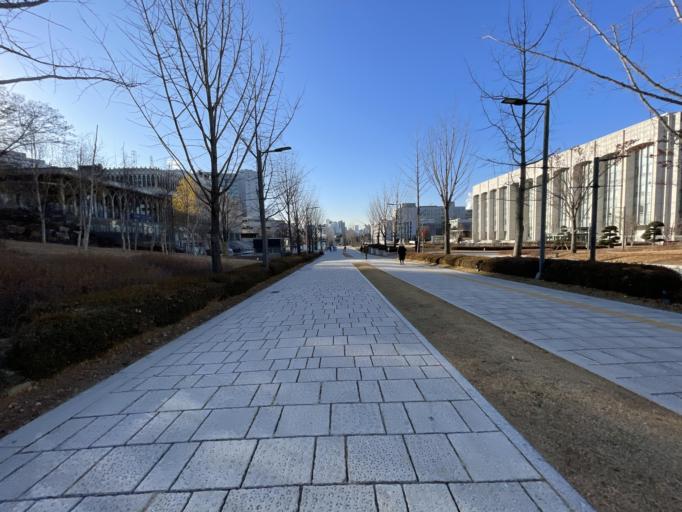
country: KR
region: Seoul
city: Seoul
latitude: 37.5644
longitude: 126.9381
